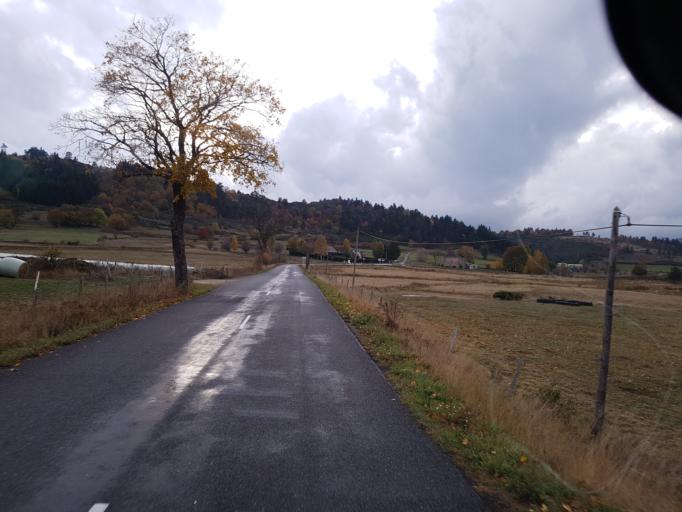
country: FR
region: Languedoc-Roussillon
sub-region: Departement de la Lozere
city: Langogne
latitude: 44.6494
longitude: 3.6819
